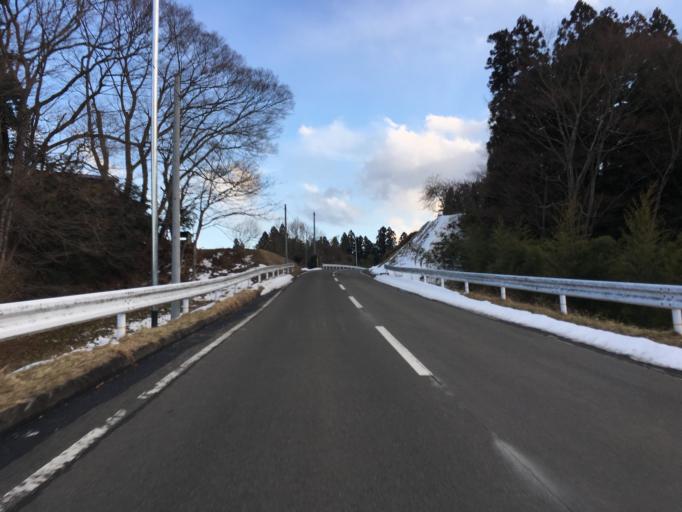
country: JP
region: Fukushima
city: Fukushima-shi
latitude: 37.6441
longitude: 140.5857
